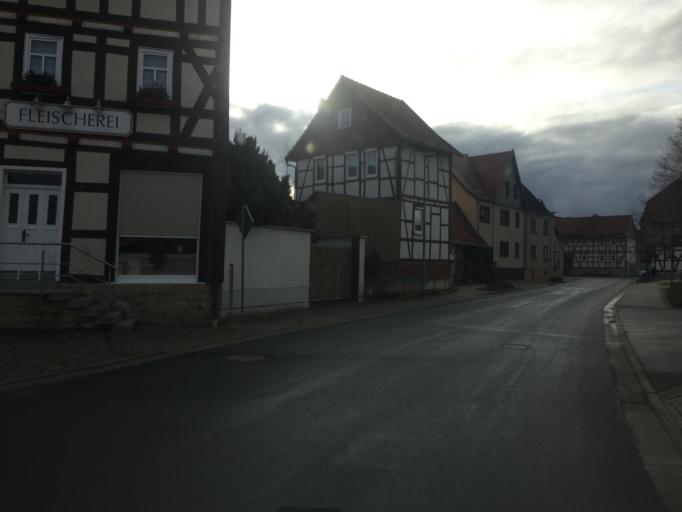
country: DE
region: Thuringia
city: Gerterode
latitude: 51.4011
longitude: 10.4760
